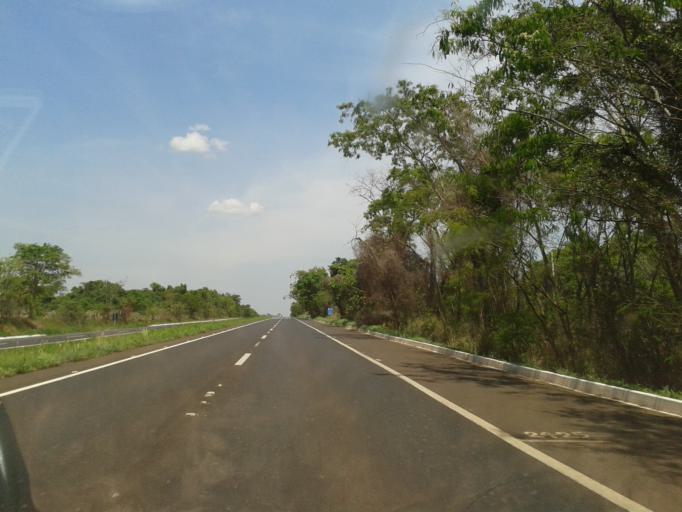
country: BR
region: Minas Gerais
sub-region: Monte Alegre De Minas
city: Monte Alegre de Minas
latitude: -18.8610
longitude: -48.7691
